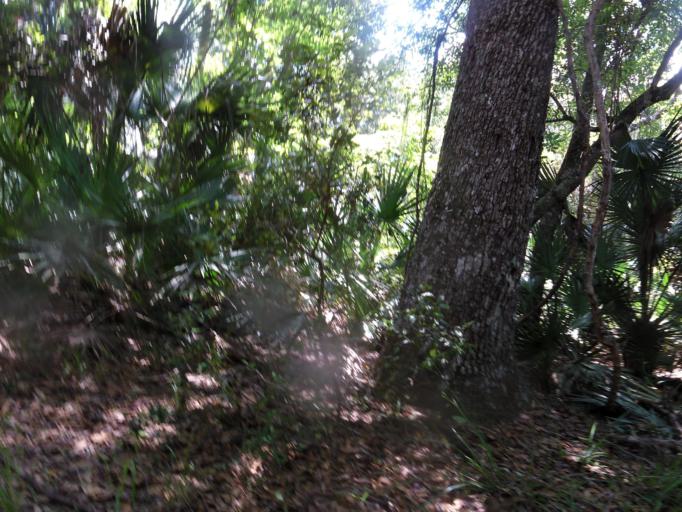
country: US
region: Florida
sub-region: Flagler County
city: Flagler Beach
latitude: 29.4154
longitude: -81.1308
